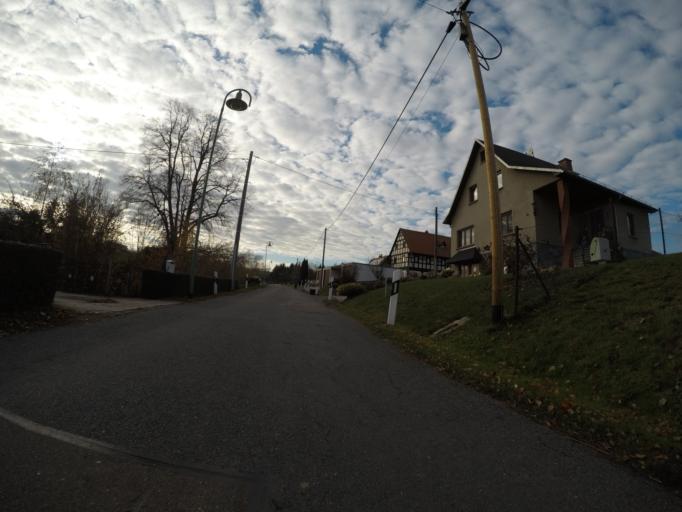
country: DE
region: Thuringia
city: Heyersdorf
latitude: 50.8471
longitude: 12.3492
